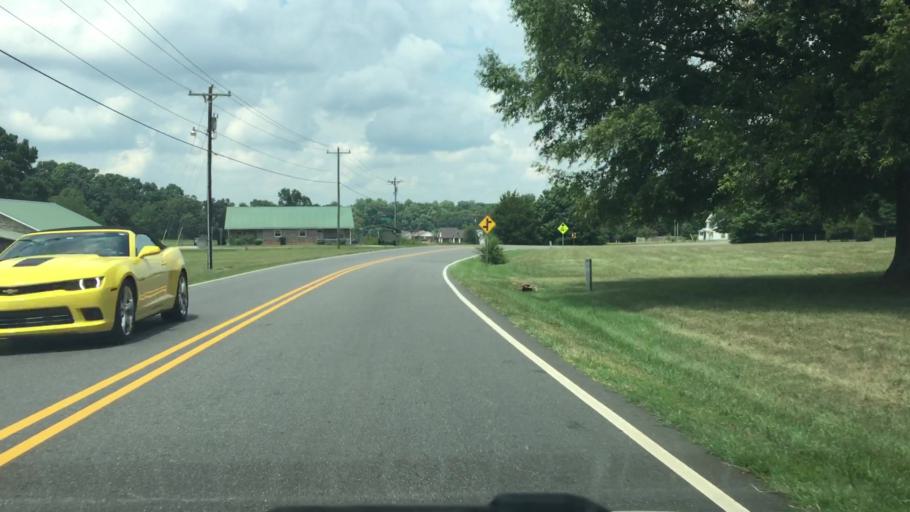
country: US
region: North Carolina
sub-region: Iredell County
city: Troutman
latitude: 35.7215
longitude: -80.8736
